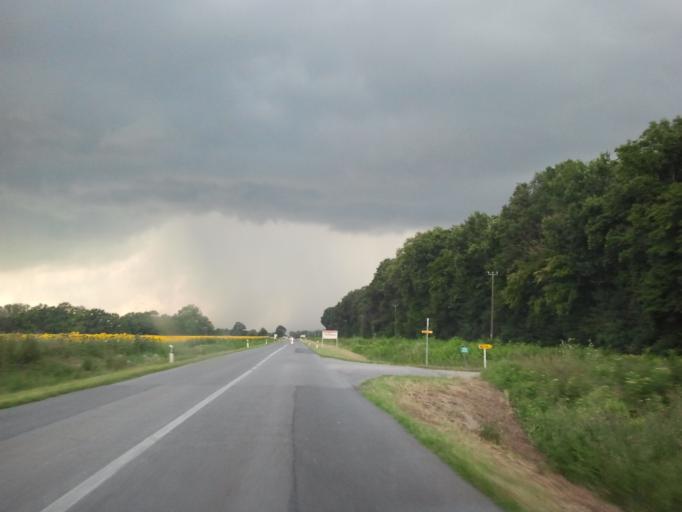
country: HR
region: Osjecko-Baranjska
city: Petrijevci
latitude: 45.6275
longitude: 18.4968
